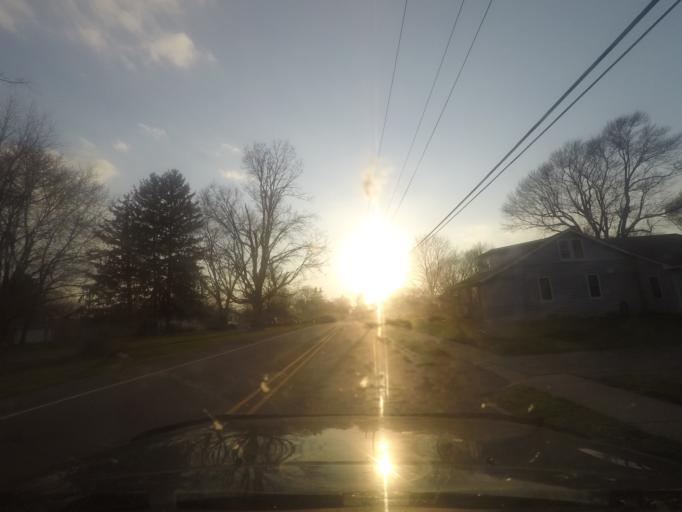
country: US
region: Indiana
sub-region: LaPorte County
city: LaPorte
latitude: 41.5913
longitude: -86.7240
